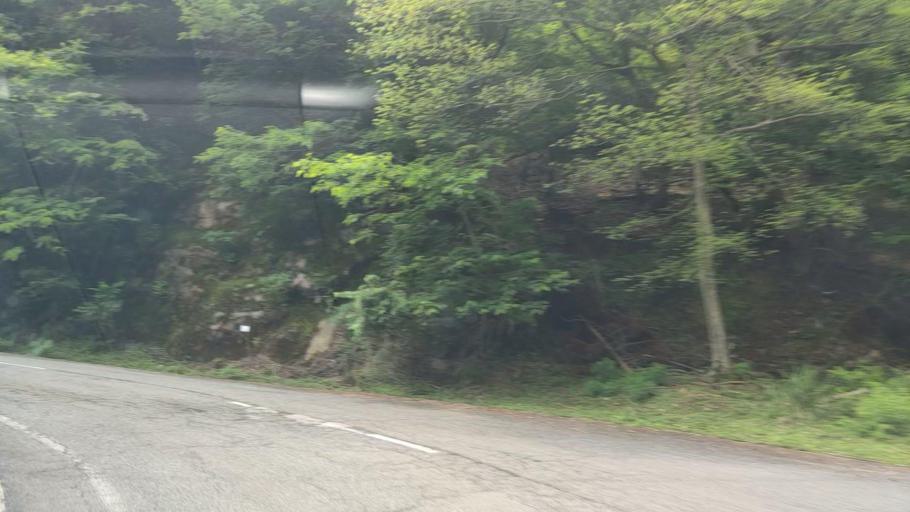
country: JP
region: Hyogo
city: Toyooka
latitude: 35.5211
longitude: 134.6942
